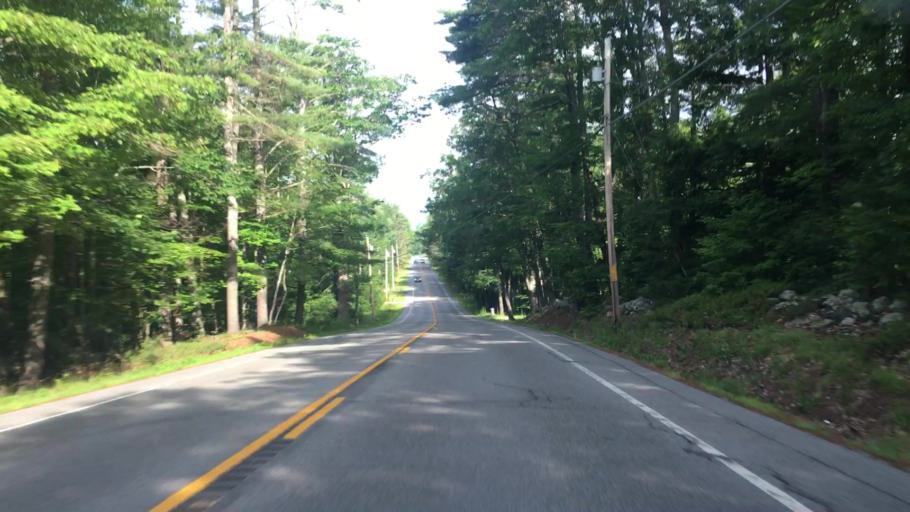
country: US
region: Maine
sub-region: York County
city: Limington
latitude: 43.7785
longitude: -70.7466
